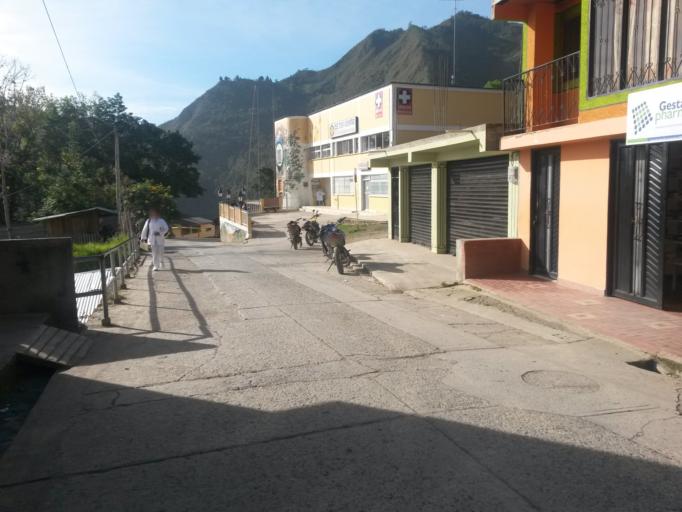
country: CO
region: Cauca
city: Inza
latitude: 2.5490
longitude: -76.0624
